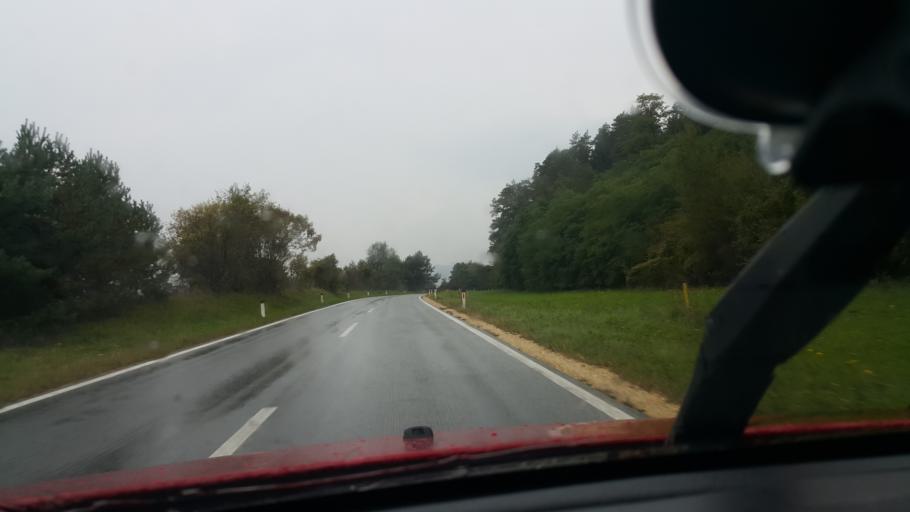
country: AT
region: Carinthia
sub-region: Politischer Bezirk Volkermarkt
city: Neuhaus
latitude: 46.6537
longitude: 14.8924
